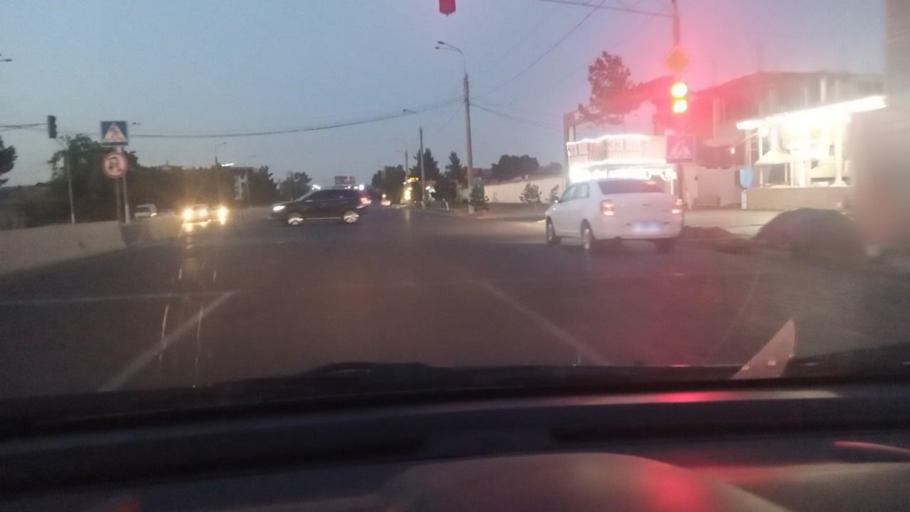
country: UZ
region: Toshkent Shahri
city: Tashkent
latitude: 41.2490
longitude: 69.2178
